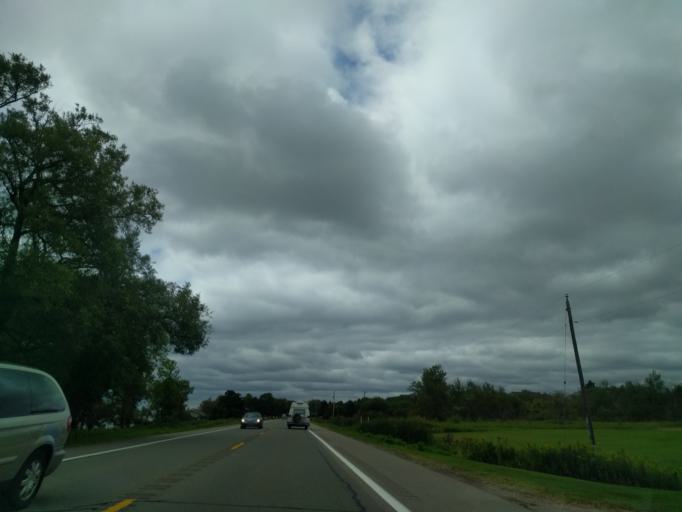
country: US
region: Michigan
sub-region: Menominee County
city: Menominee
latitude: 45.2481
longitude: -87.4897
